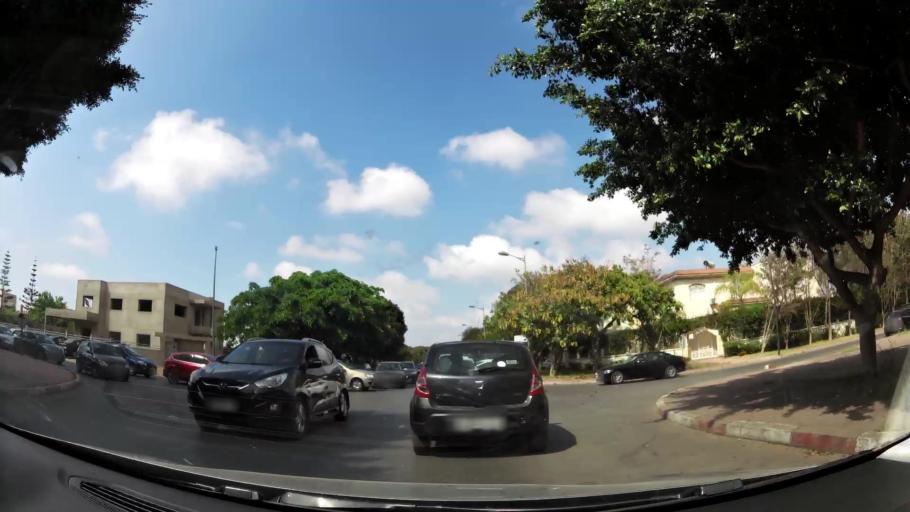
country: MA
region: Rabat-Sale-Zemmour-Zaer
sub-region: Skhirate-Temara
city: Temara
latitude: 33.9634
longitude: -6.8648
